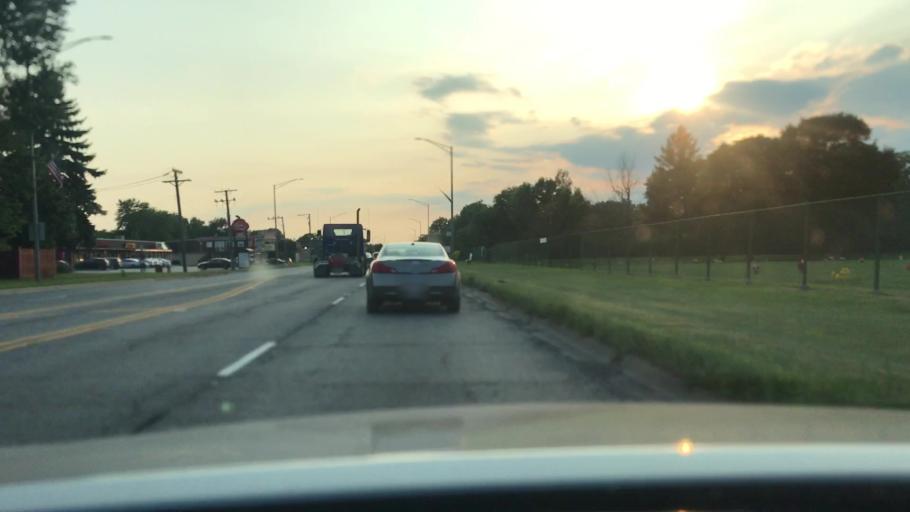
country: US
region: Illinois
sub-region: Cook County
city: Justice
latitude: 41.7476
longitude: -87.8279
